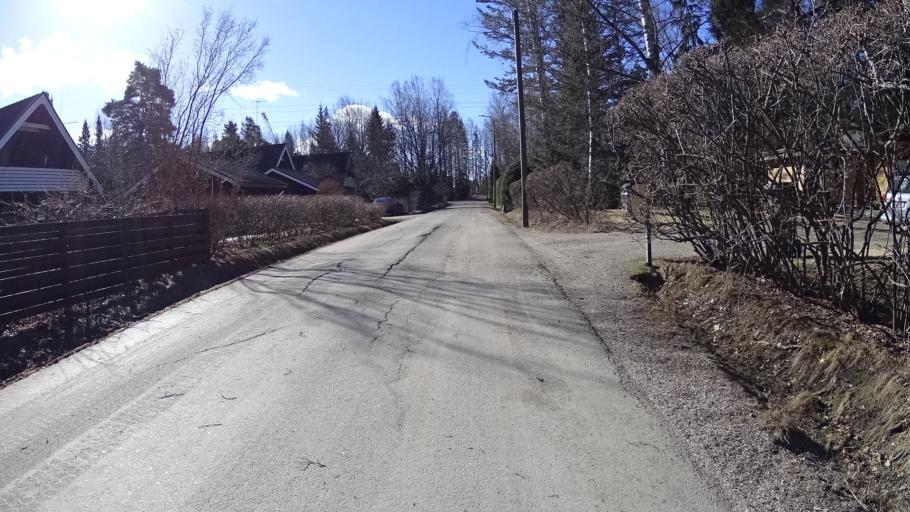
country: FI
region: Uusimaa
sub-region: Helsinki
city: Teekkarikylae
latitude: 60.2651
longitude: 24.8851
